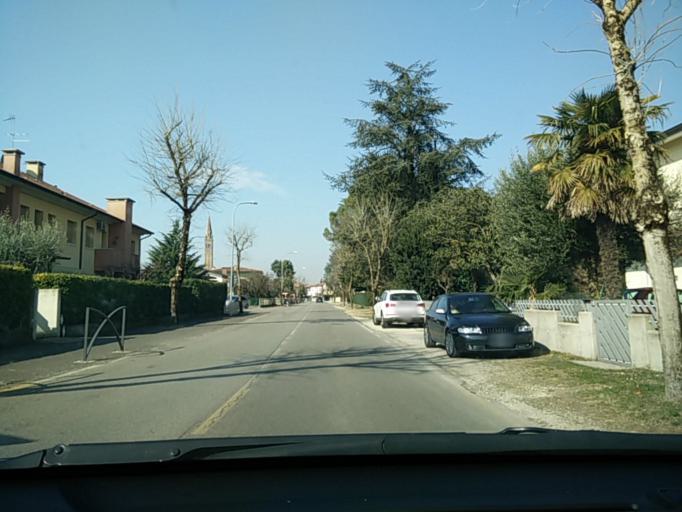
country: IT
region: Veneto
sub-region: Provincia di Treviso
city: Santa Lucia di Piave
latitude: 45.8509
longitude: 12.2924
